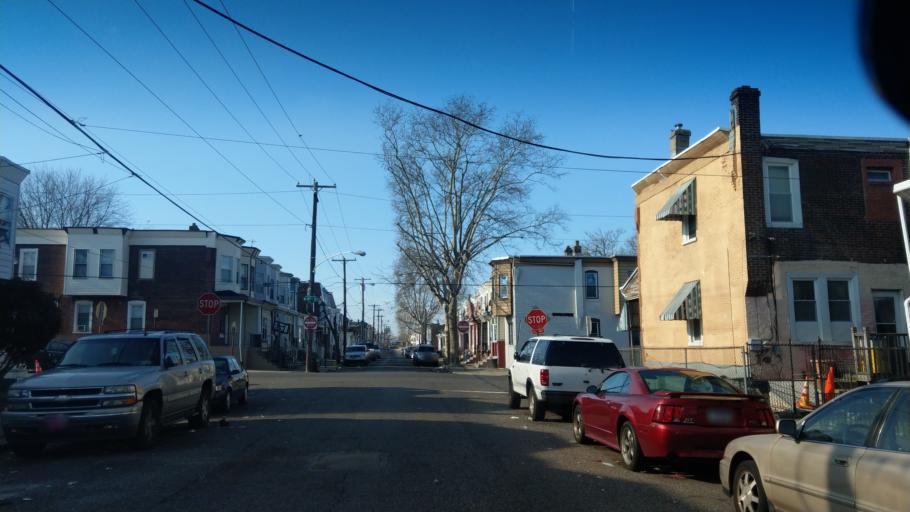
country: US
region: Pennsylvania
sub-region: Montgomery County
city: Rockledge
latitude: 40.0270
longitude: -75.1302
